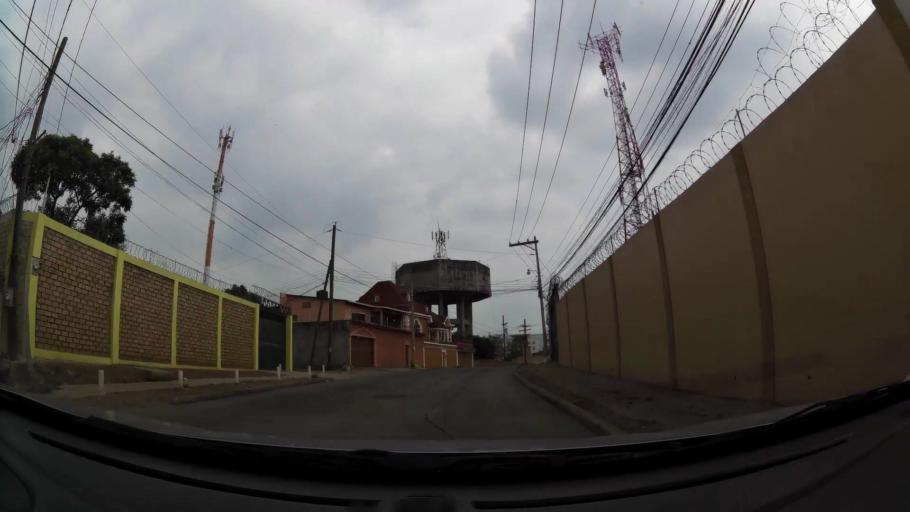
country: HN
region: Francisco Morazan
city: Tegucigalpa
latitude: 14.0941
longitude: -87.1712
